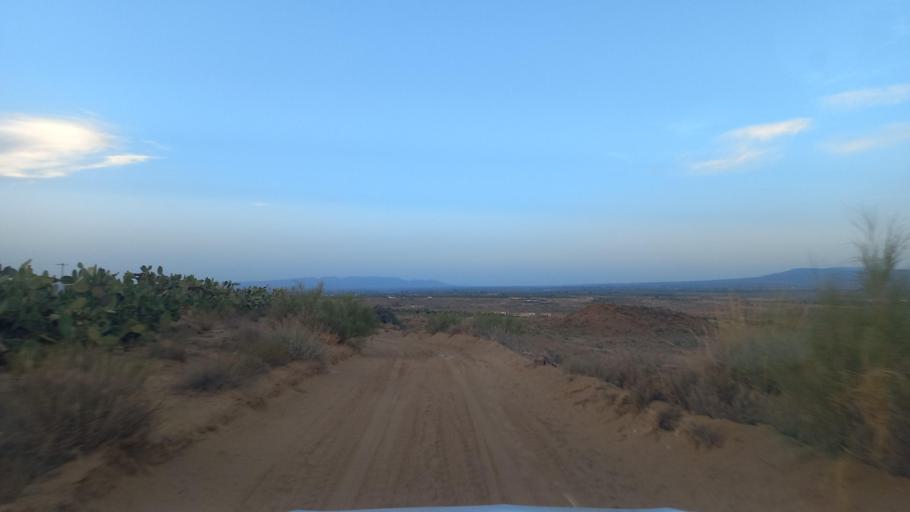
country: TN
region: Al Qasrayn
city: Kasserine
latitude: 35.1917
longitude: 9.0498
